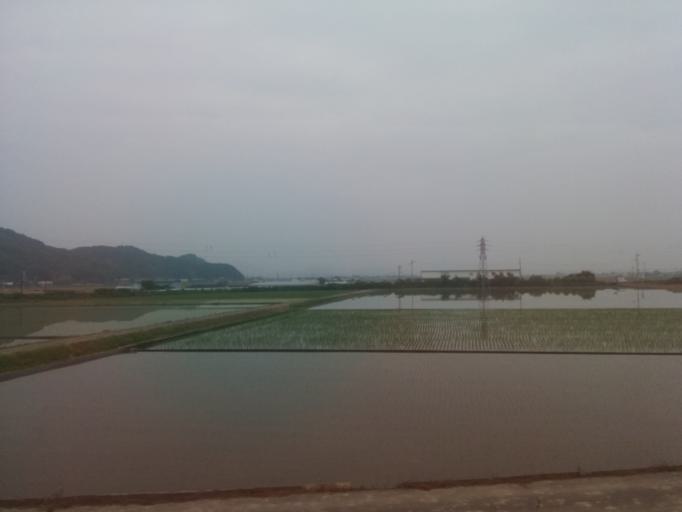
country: JP
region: Shiga Prefecture
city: Omihachiman
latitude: 35.1599
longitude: 136.1515
